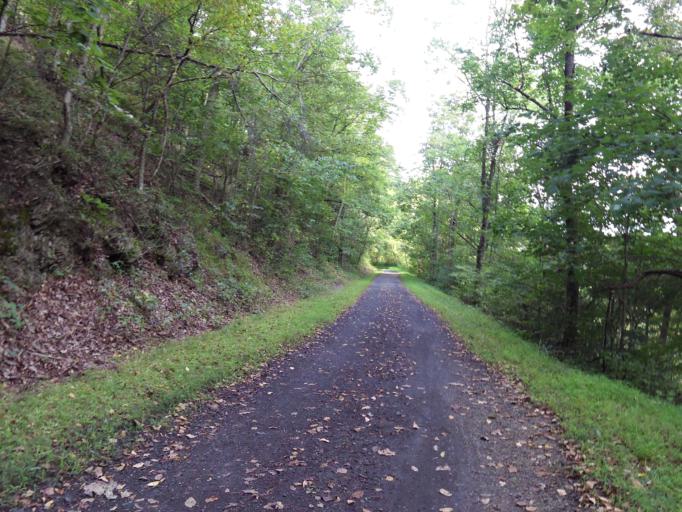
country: US
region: Virginia
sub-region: Washington County
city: Abingdon
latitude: 36.6812
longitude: -81.9439
